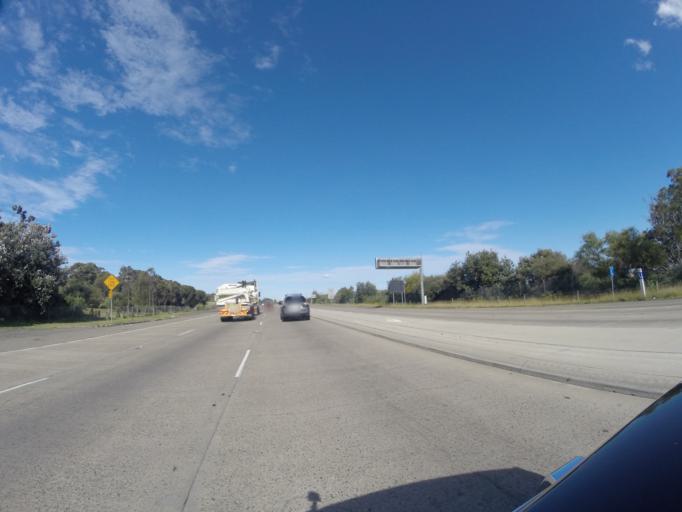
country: AU
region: New South Wales
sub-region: Botany Bay
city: Botany
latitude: -33.9470
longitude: 151.1893
